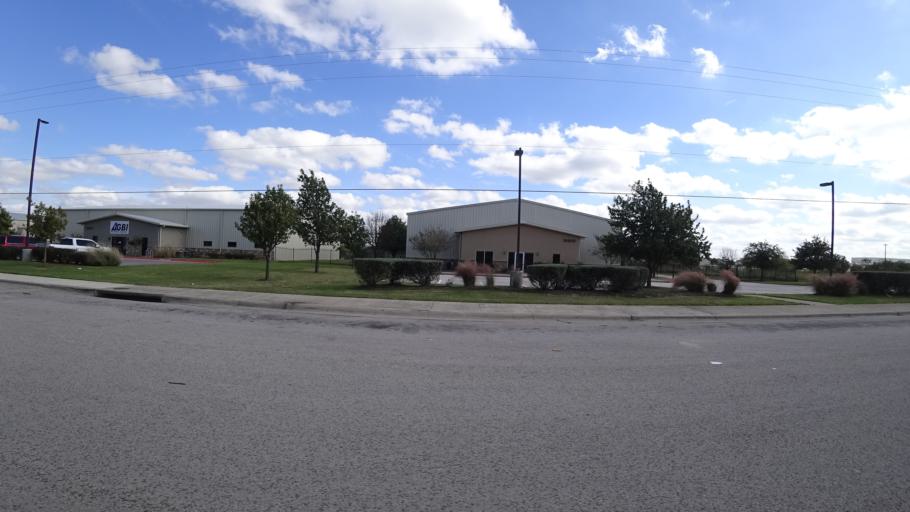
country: US
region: Texas
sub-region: Travis County
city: Windemere
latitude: 30.4685
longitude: -97.6630
